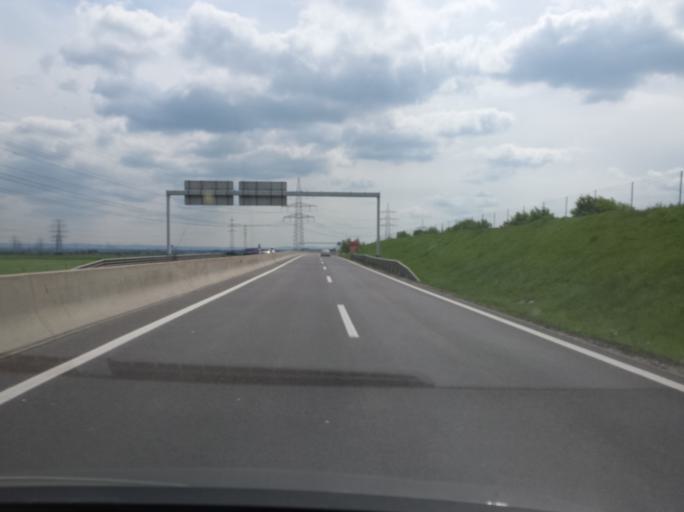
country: AT
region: Lower Austria
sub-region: Politischer Bezirk Wien-Umgebung
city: Leopoldsdorf
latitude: 48.1177
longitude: 16.4129
